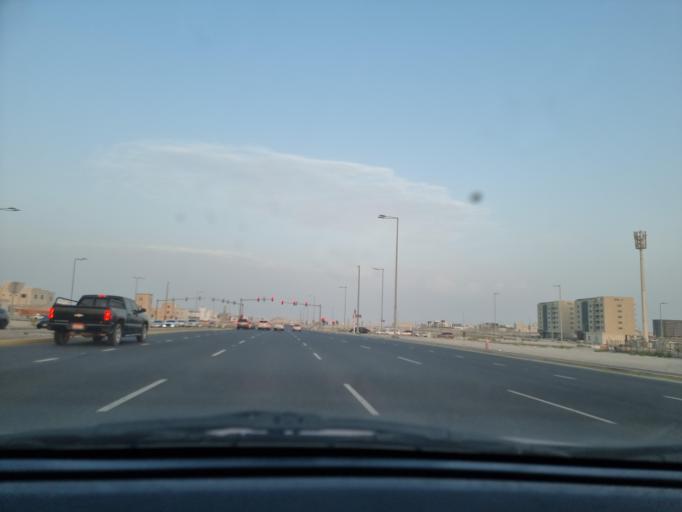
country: AE
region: Abu Dhabi
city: Abu Dhabi
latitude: 24.3738
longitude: 54.7386
